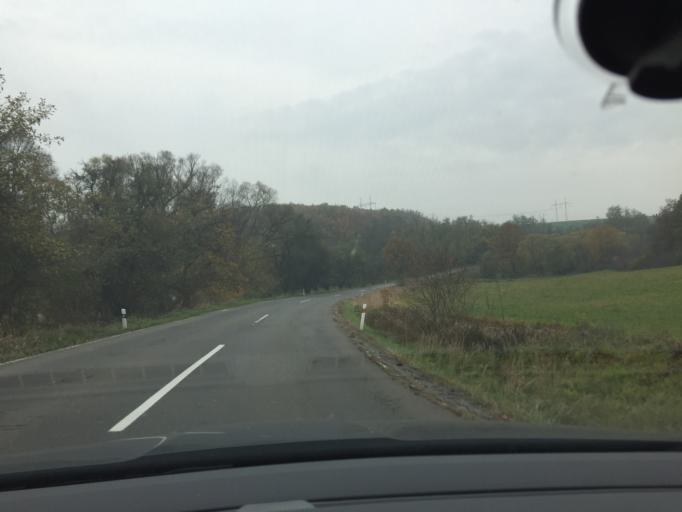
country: SK
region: Banskobystricky
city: Velky Krtis
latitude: 48.2770
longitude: 19.4766
